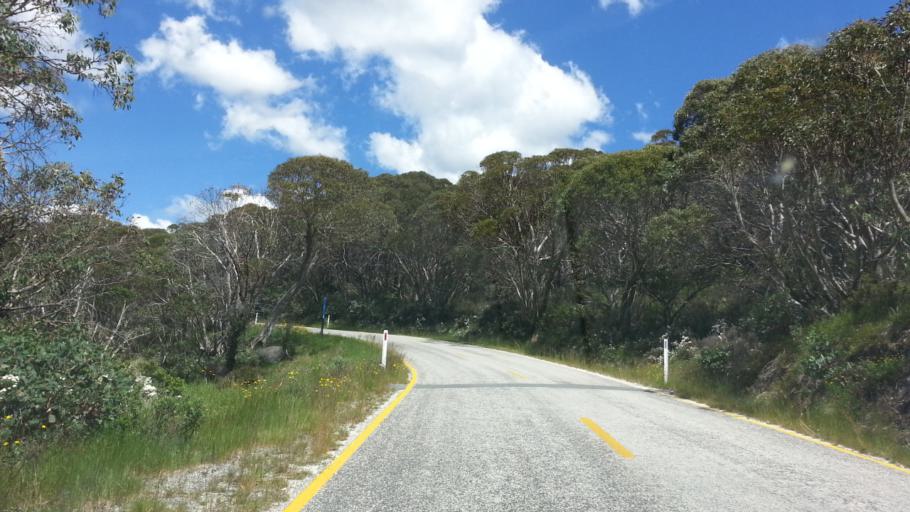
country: AU
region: Victoria
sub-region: Alpine
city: Mount Beauty
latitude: -36.8715
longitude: 147.2863
